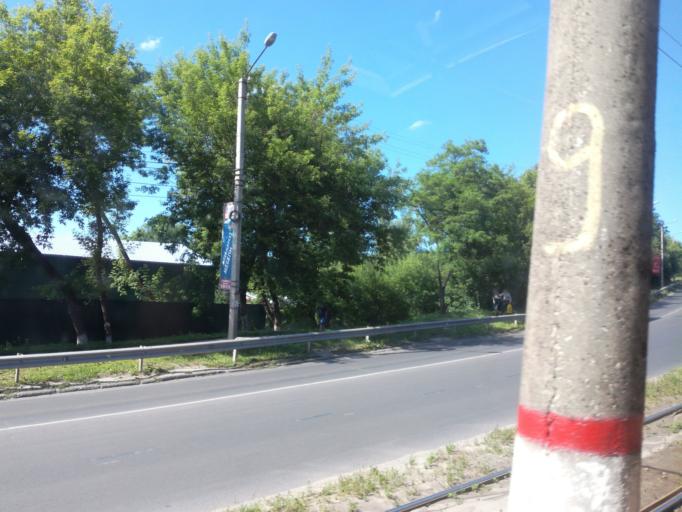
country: RU
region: Kursk
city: Kursk
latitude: 51.7467
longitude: 36.1707
